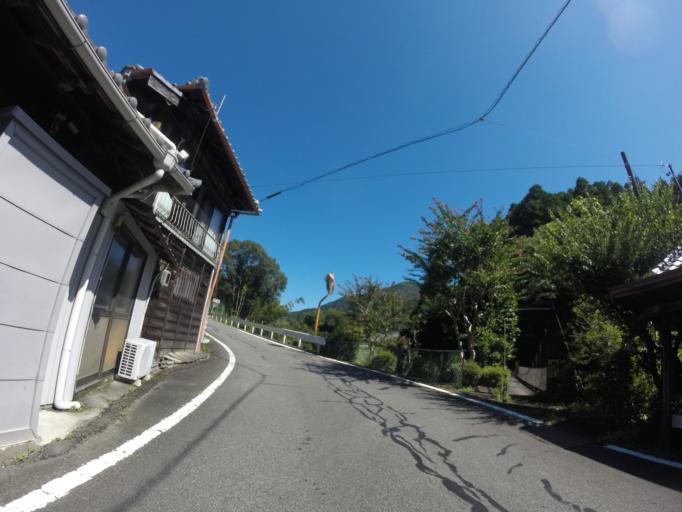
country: JP
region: Shizuoka
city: Kanaya
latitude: 34.9274
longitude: 138.1399
